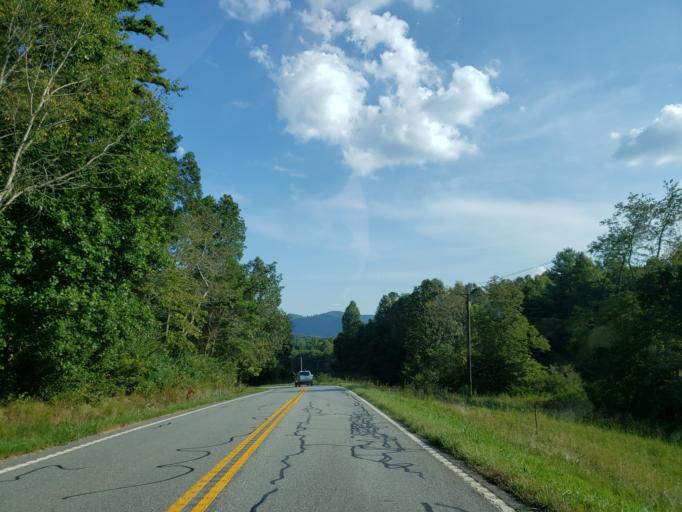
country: US
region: Georgia
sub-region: Fannin County
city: Blue Ridge
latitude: 34.8506
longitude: -84.2188
